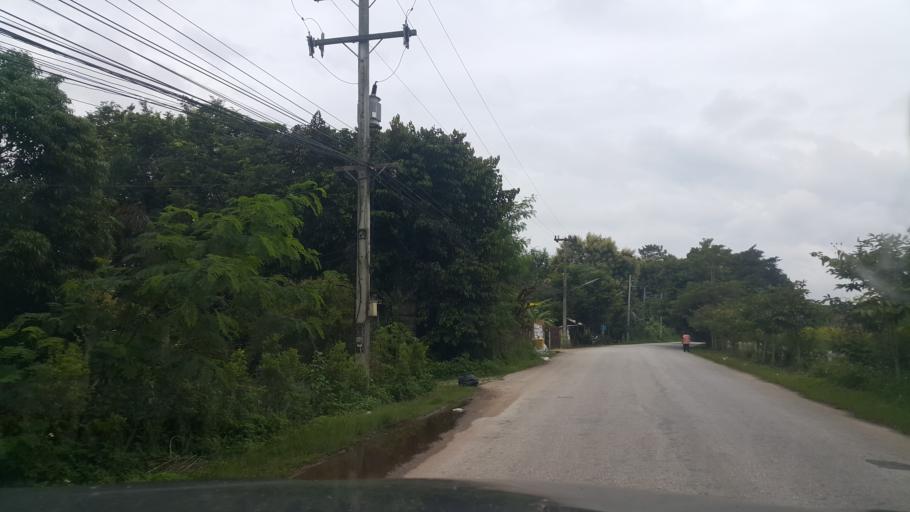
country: TH
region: Chiang Mai
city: San Sai
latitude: 18.9187
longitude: 99.0250
